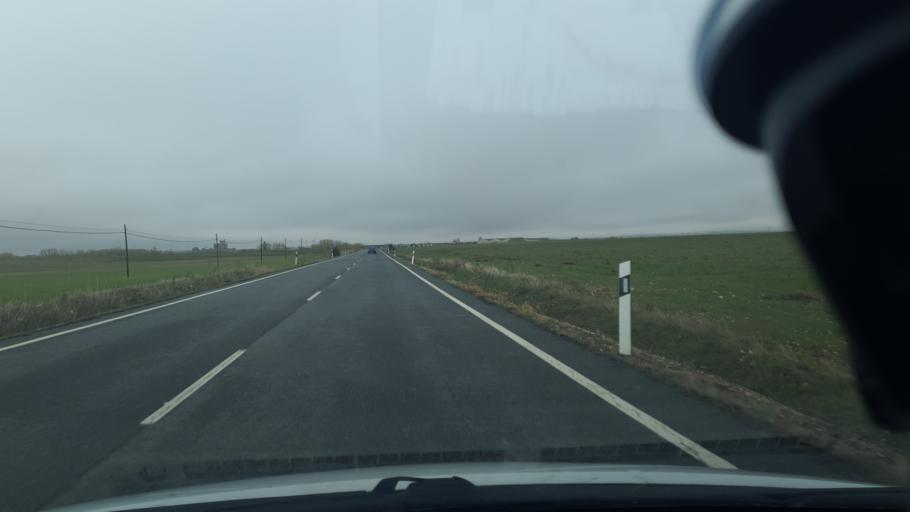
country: ES
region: Castille and Leon
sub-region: Provincia de Segovia
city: Turegano
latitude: 41.1509
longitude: -4.0270
